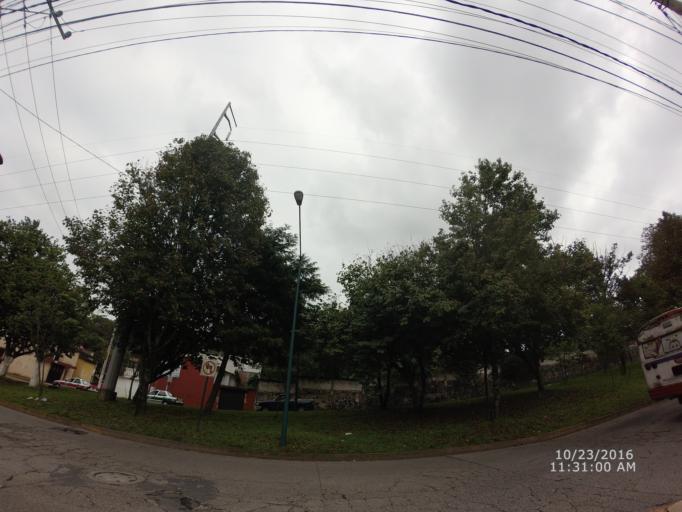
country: MX
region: Veracruz
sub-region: Tlalnelhuayocan
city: Guadalupe Victoria
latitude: 19.5495
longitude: -96.9379
